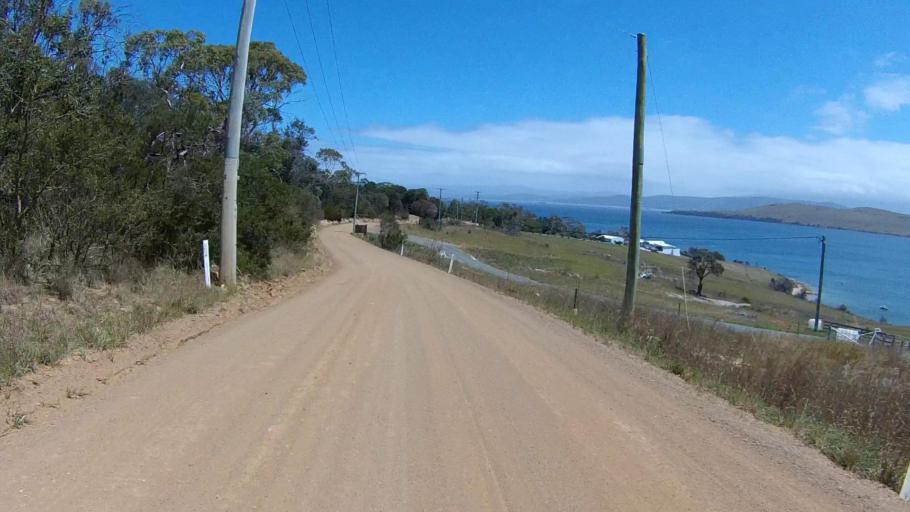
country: AU
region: Tasmania
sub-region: Clarence
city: Lauderdale
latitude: -42.9330
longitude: 147.4660
